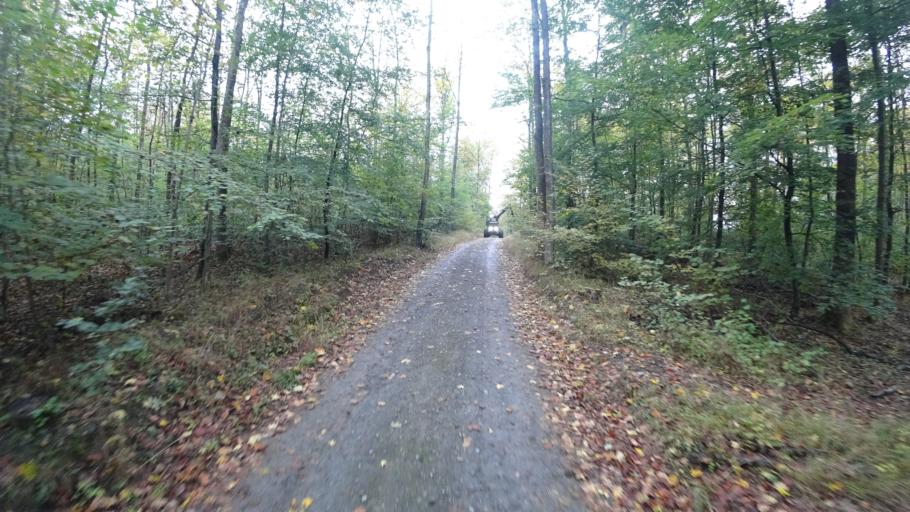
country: DE
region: Rheinland-Pfalz
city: Ruckeroth
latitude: 50.5601
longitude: 7.7663
